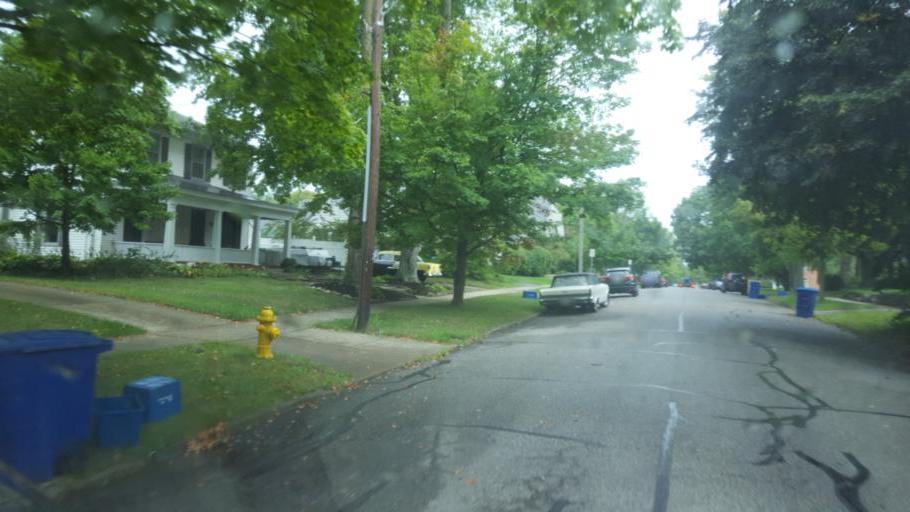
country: US
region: Ohio
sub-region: Delaware County
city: Delaware
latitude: 40.3045
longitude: -83.0691
